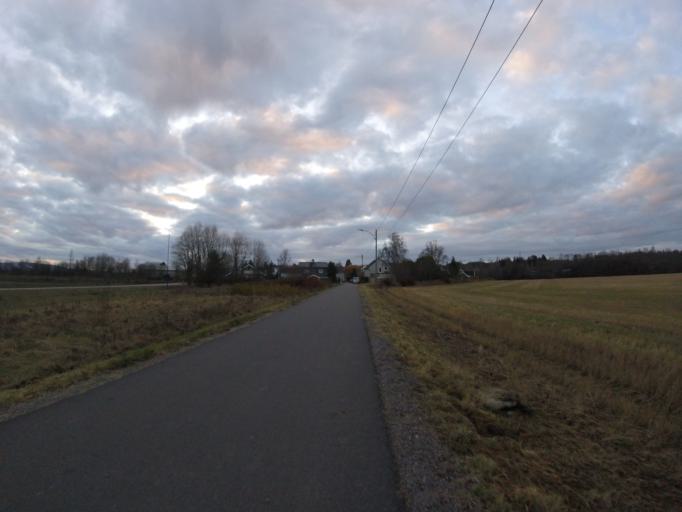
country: NO
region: Akershus
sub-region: Skedsmo
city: Leirsund
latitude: 59.9985
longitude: 11.0918
